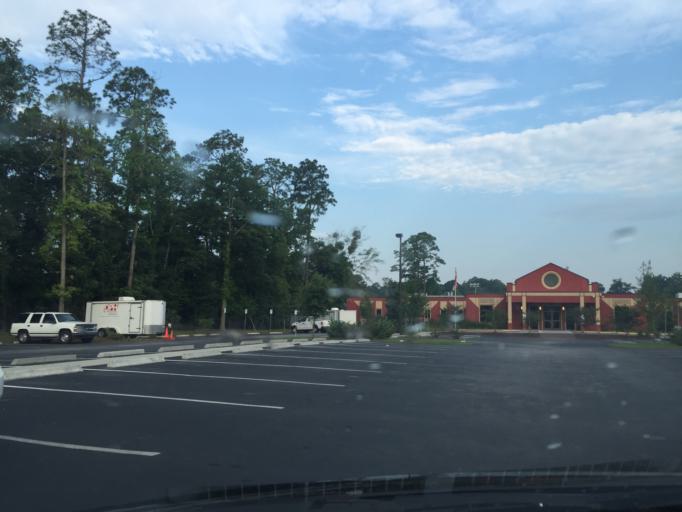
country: US
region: Georgia
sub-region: Chatham County
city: Isle of Hope
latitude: 32.0027
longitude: -81.0908
